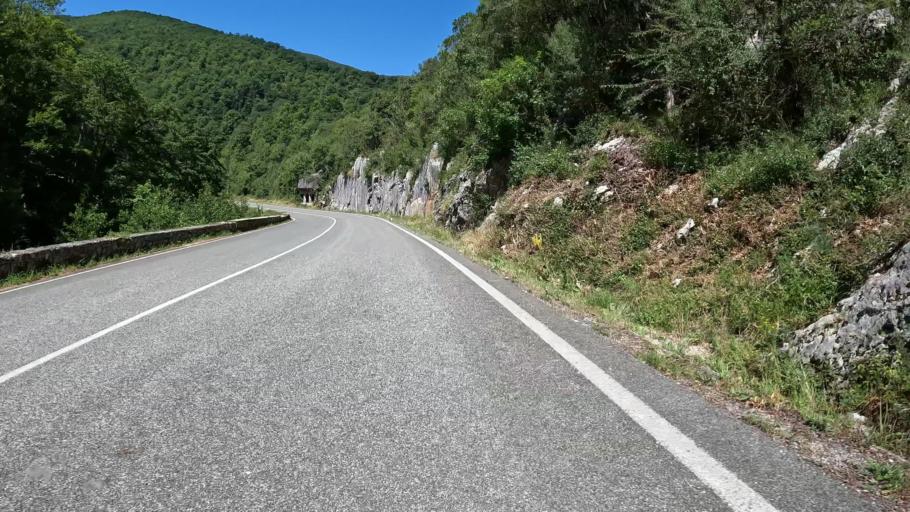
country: ES
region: Basque Country
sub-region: Provincia de Guipuzcoa
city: Oreja
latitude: 43.0710
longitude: -2.0075
